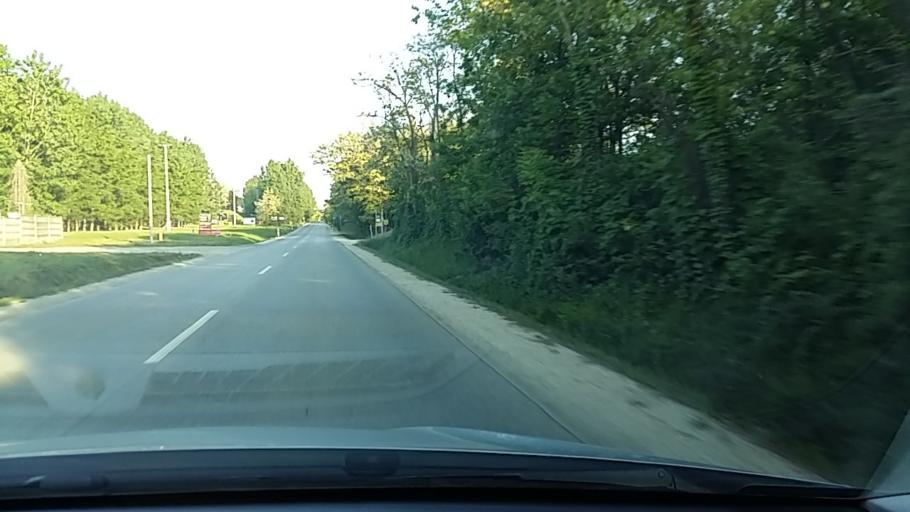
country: HU
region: Pest
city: Orbottyan
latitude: 47.6945
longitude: 19.2505
